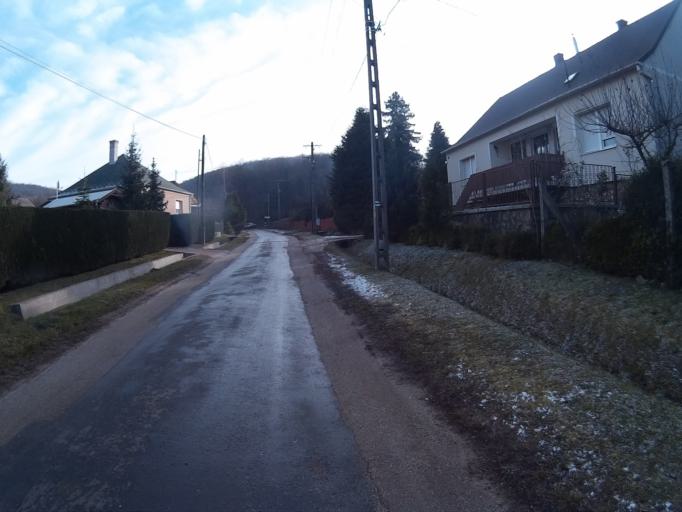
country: HU
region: Komarom-Esztergom
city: Oroszlany
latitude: 47.4720
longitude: 18.3983
